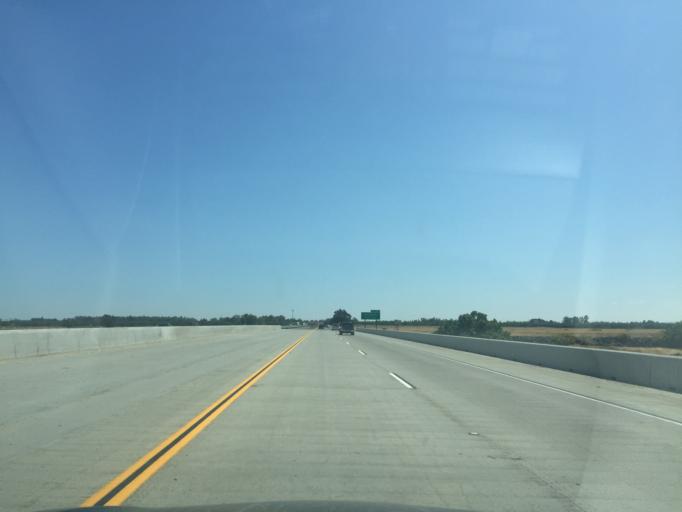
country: US
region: California
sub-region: Tehama County
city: Corning
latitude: 39.9755
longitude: -122.2019
